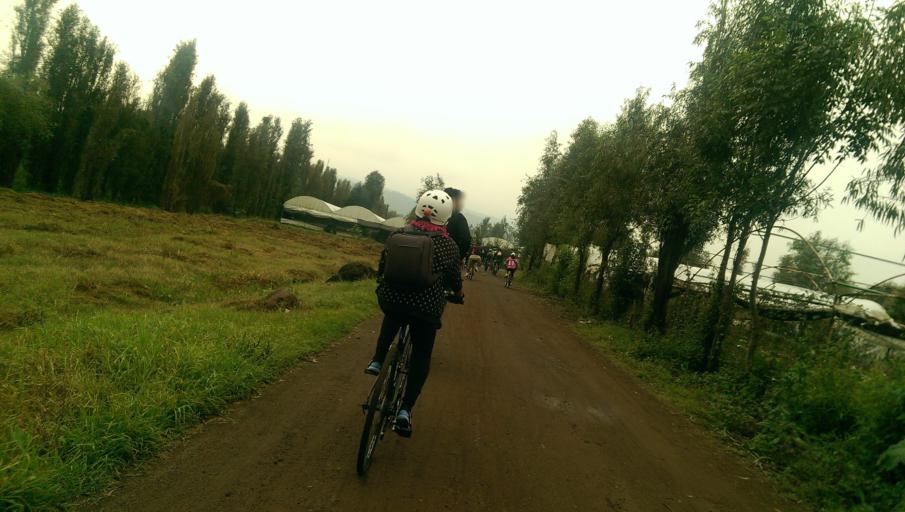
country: MX
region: Mexico City
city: Xochimilco
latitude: 19.2656
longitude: -99.0728
